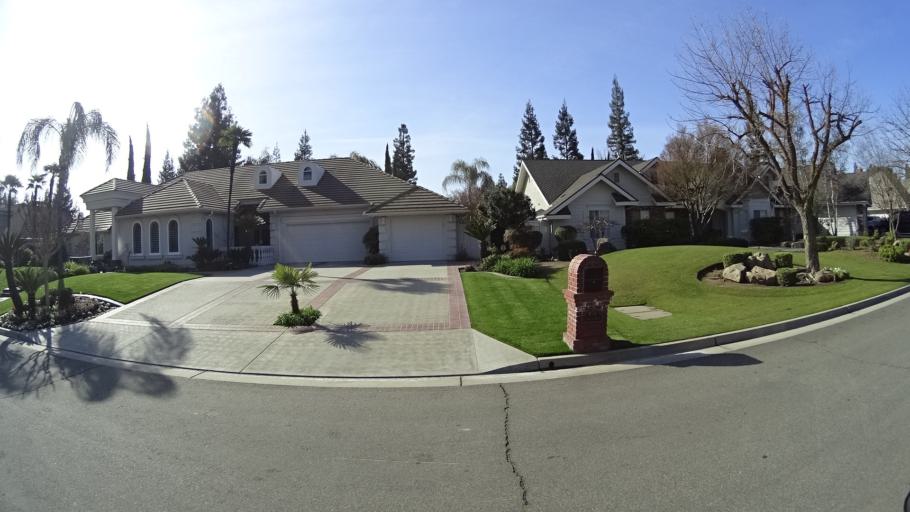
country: US
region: California
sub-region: Fresno County
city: Clovis
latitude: 36.8788
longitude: -119.7673
